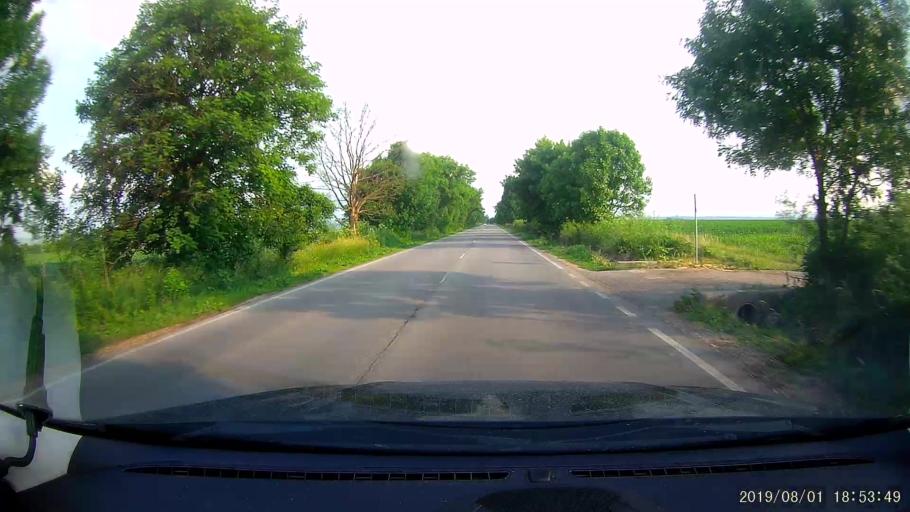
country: BG
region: Shumen
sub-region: Obshtina Shumen
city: Shumen
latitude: 43.2139
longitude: 26.9979
